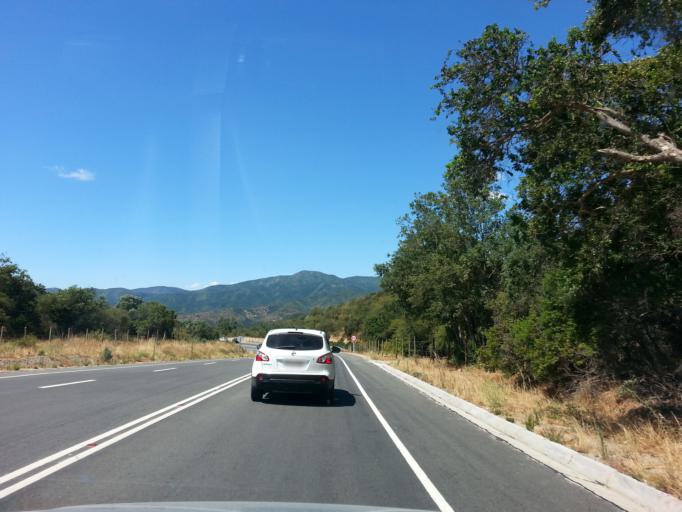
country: CL
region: Valparaiso
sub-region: Provincia de Marga Marga
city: Villa Alemana
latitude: -33.1699
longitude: -71.3519
